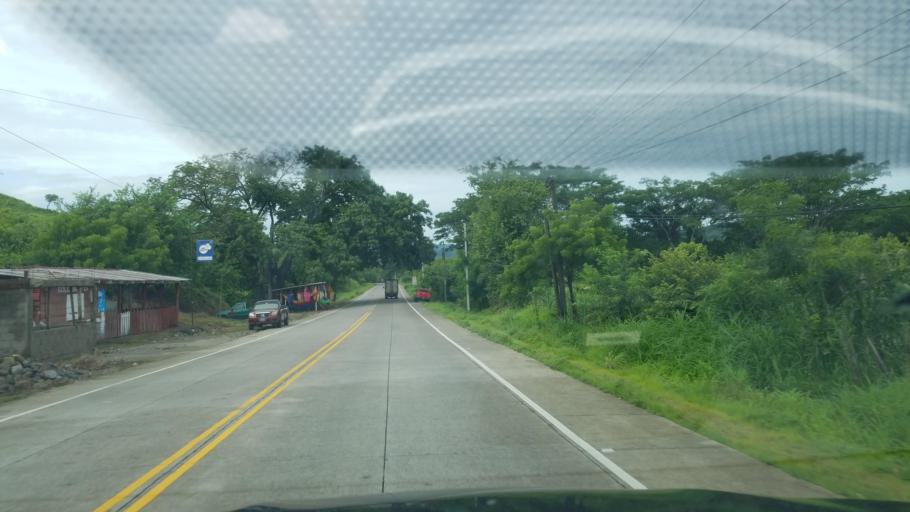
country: HN
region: Choluteca
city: Pespire
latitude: 13.6417
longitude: -87.3688
